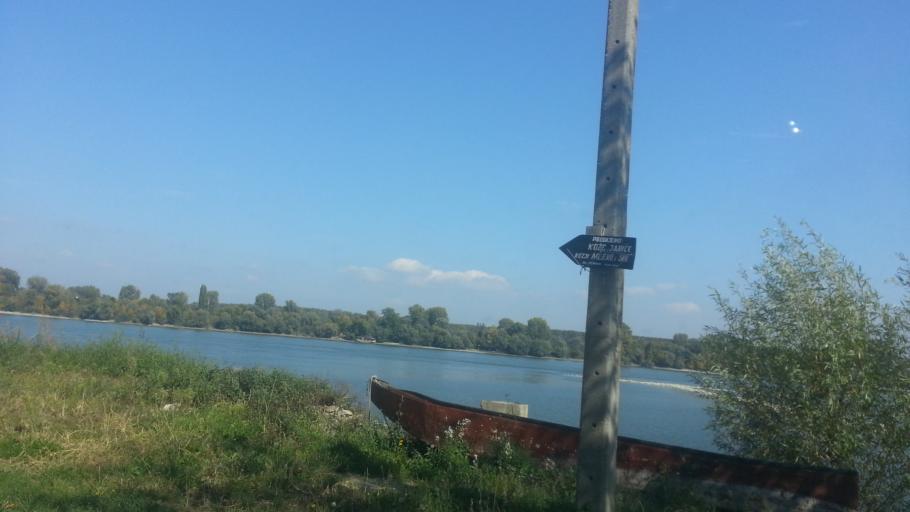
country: RS
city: Novi Slankamen
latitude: 45.1449
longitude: 20.2563
